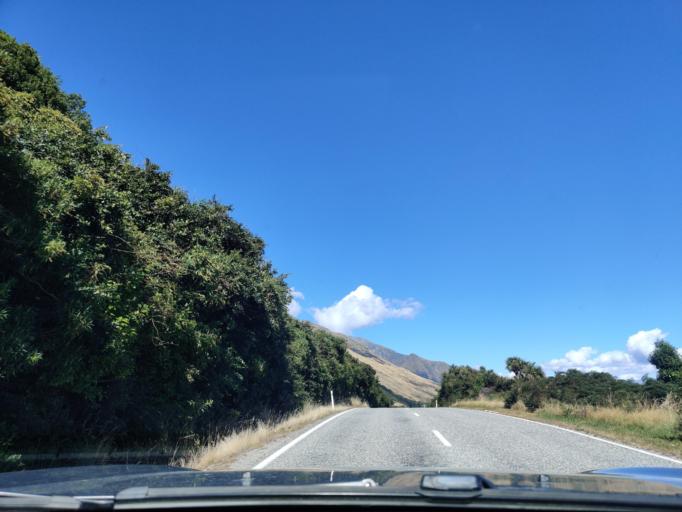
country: NZ
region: Otago
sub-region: Queenstown-Lakes District
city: Queenstown
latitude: -44.9409
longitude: 168.4314
